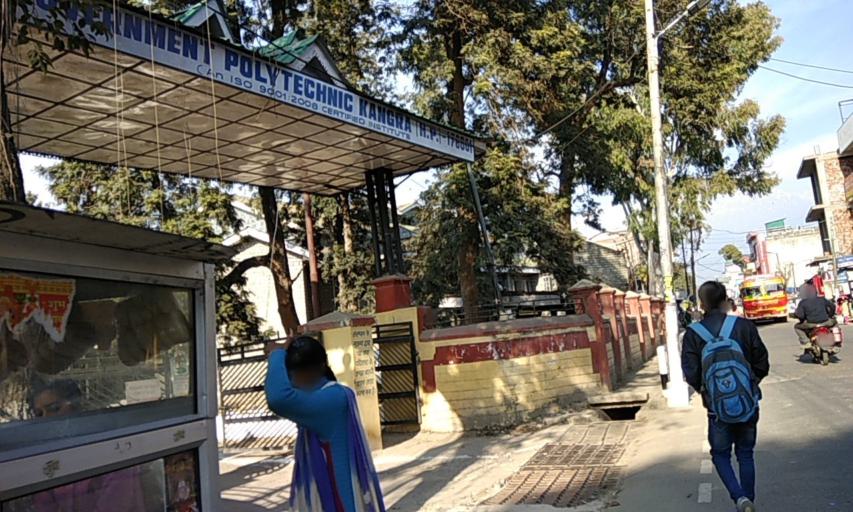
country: IN
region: Himachal Pradesh
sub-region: Kangra
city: Kangra
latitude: 32.1084
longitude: 76.2766
